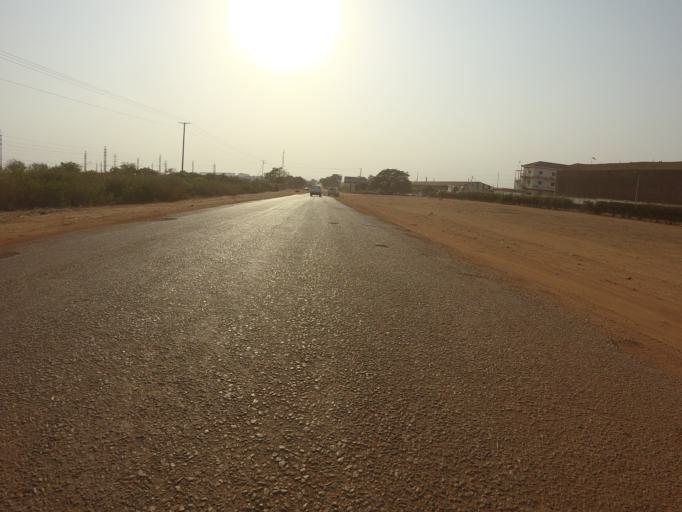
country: GH
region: Greater Accra
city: Tema
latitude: 5.6700
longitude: 0.0173
